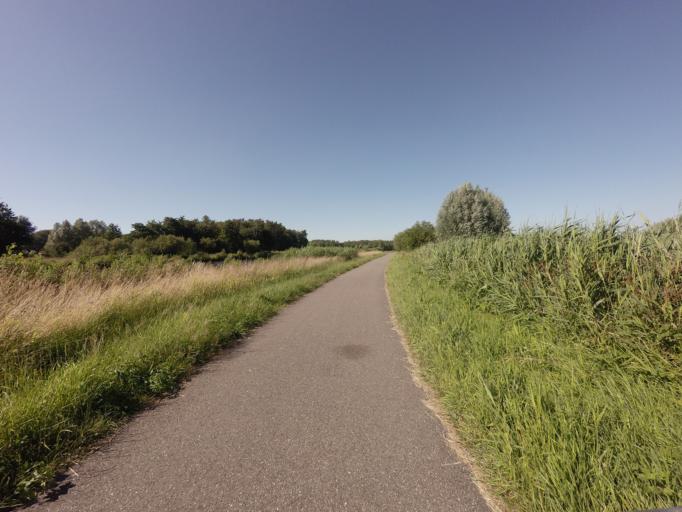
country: NL
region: South Holland
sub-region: Bodegraven-Reeuwijk
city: Bodegraven
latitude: 52.0602
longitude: 4.7466
